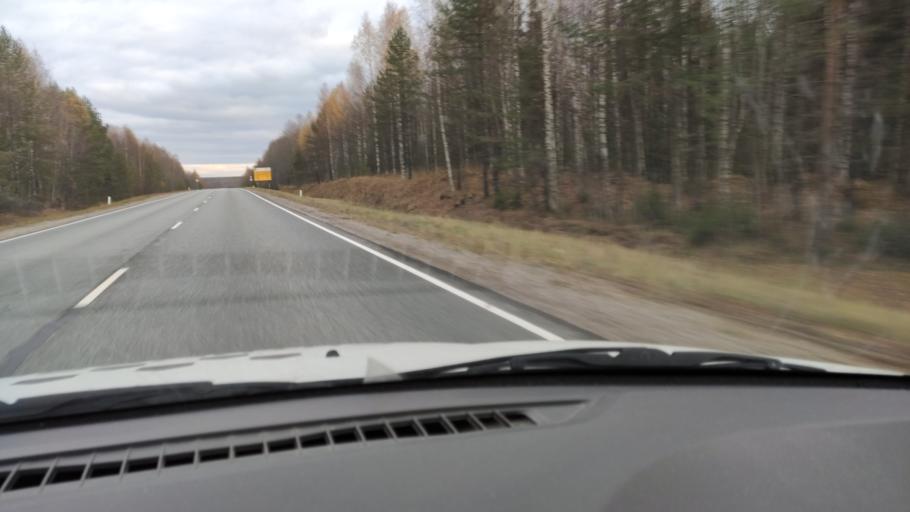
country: RU
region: Kirov
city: Dubrovka
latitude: 58.8959
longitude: 51.3250
